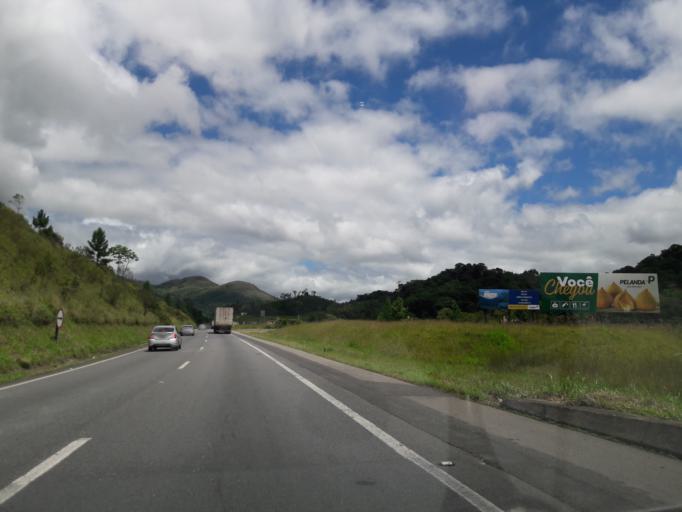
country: BR
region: Parana
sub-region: Antonina
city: Antonina
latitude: -25.1070
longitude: -48.7877
